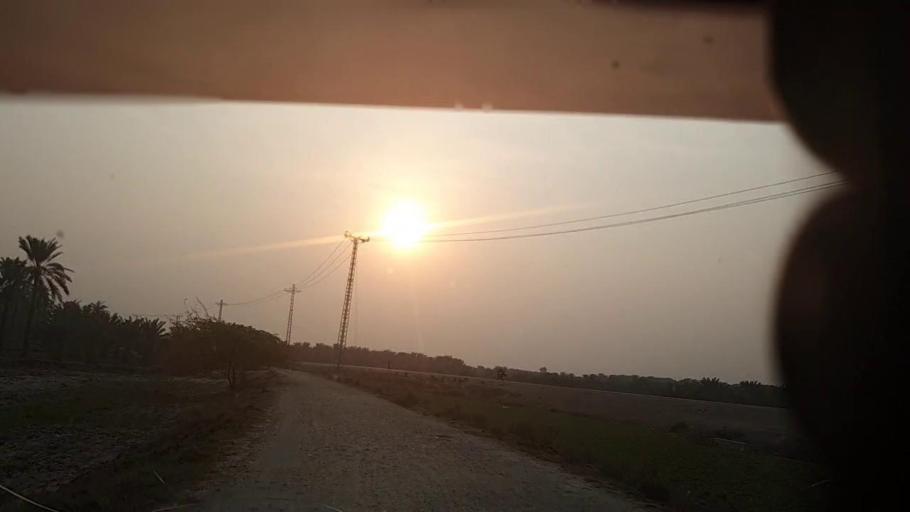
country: PK
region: Sindh
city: Pir jo Goth
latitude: 27.5221
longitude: 68.6406
